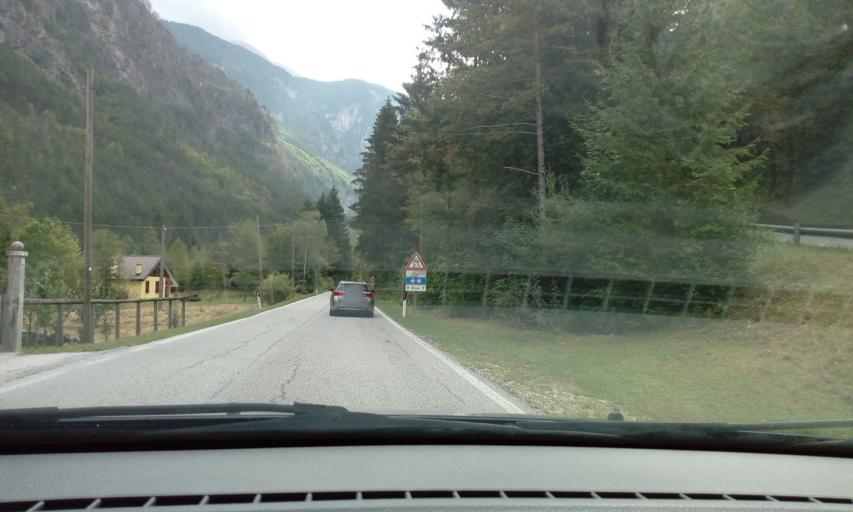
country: IT
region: Friuli Venezia Giulia
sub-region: Provincia di Udine
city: Chiusaforte
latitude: 46.4018
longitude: 13.3992
